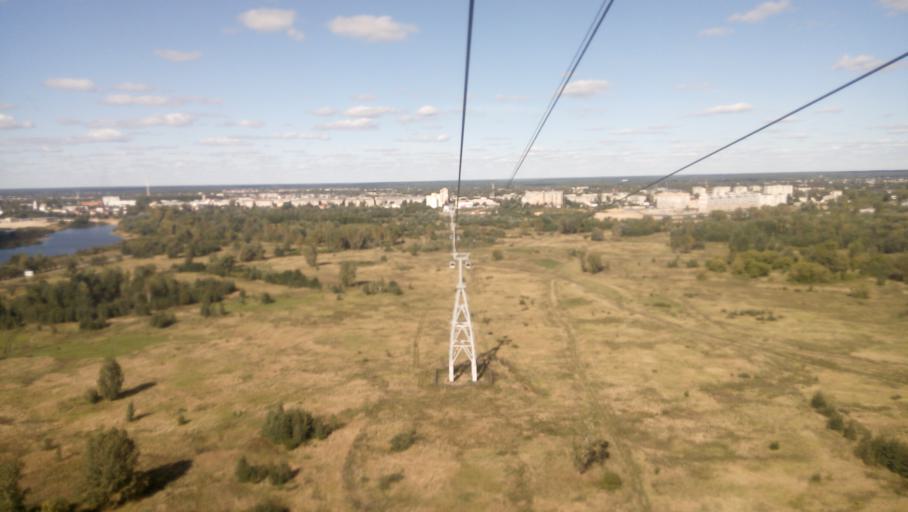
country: RU
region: Nizjnij Novgorod
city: Bor
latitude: 56.3414
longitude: 44.0520
